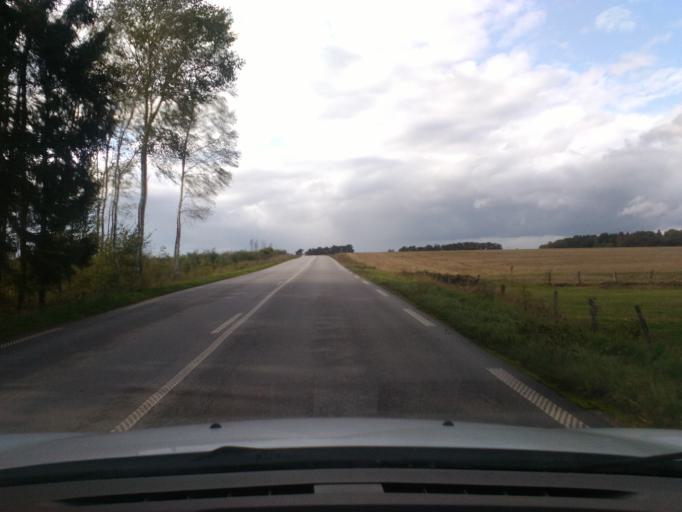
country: FR
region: Lorraine
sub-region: Departement des Vosges
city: Aydoilles
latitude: 48.2417
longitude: 6.6455
